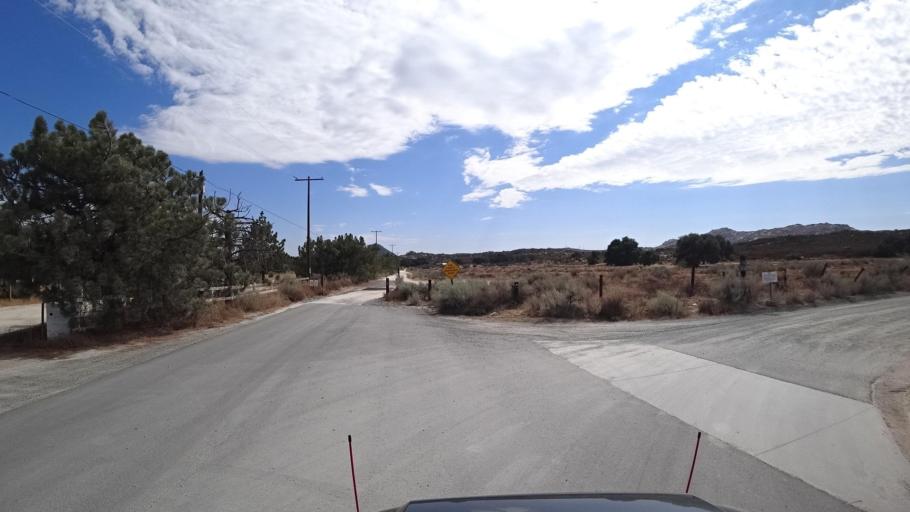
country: MX
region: Baja California
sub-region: Tecate
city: Cereso del Hongo
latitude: 32.6395
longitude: -116.2727
